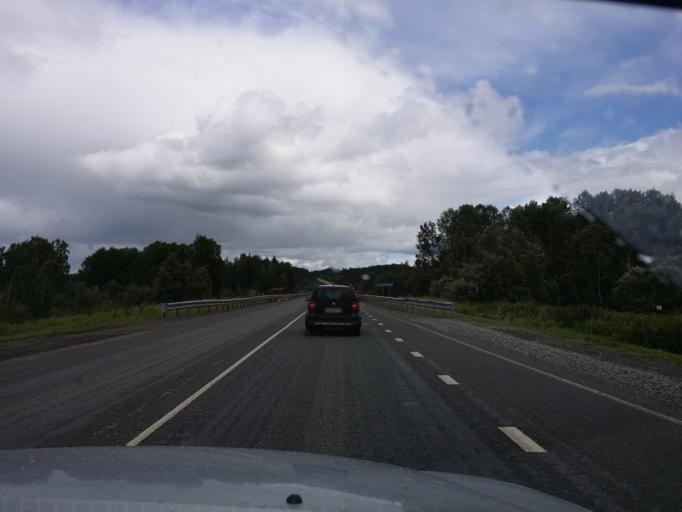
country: RU
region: Tjumen
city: Abalak
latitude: 58.4673
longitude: 68.5338
